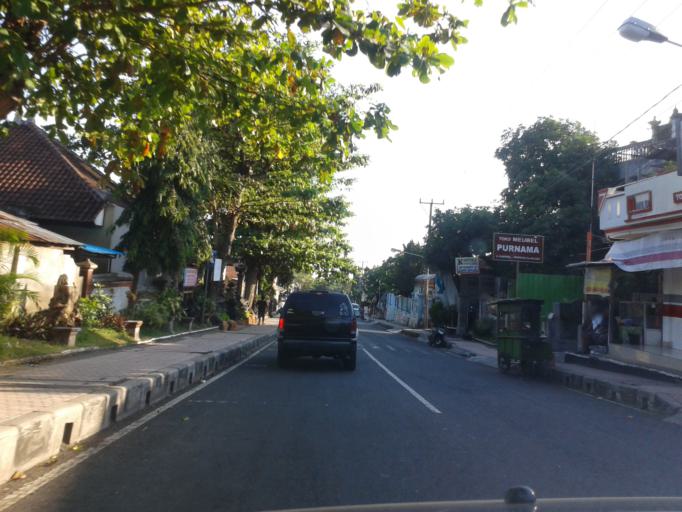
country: ID
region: Bali
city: Semarapura
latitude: -8.5317
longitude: 115.4044
